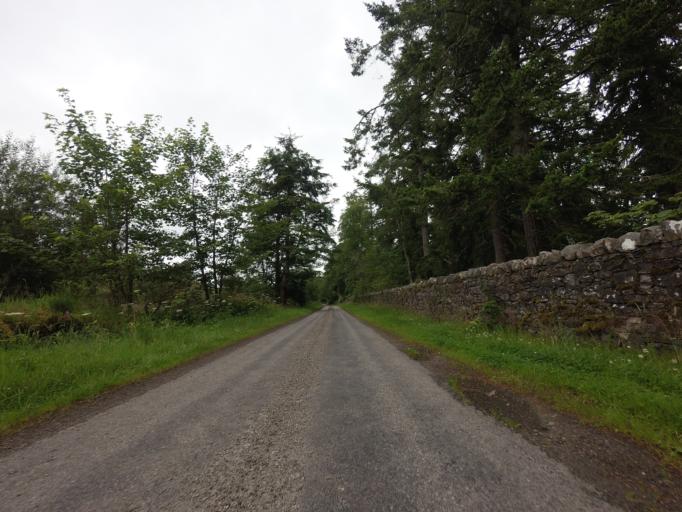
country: GB
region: Scotland
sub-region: Highland
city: Evanton
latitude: 57.8908
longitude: -4.3782
